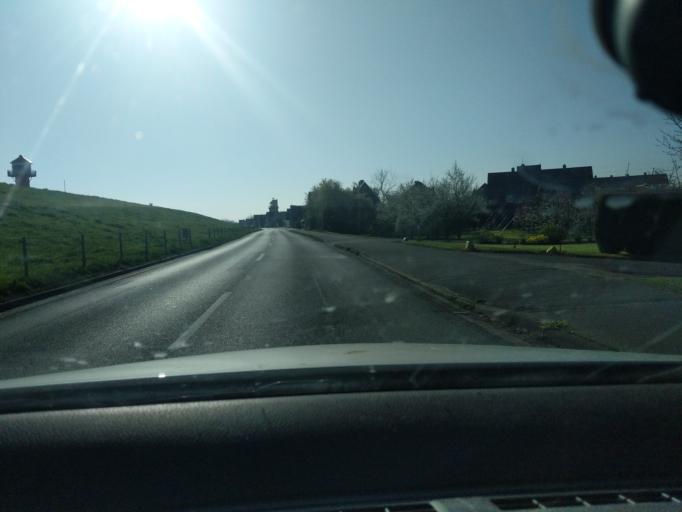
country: DE
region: Lower Saxony
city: Grunendeich
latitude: 53.5697
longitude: 9.6376
